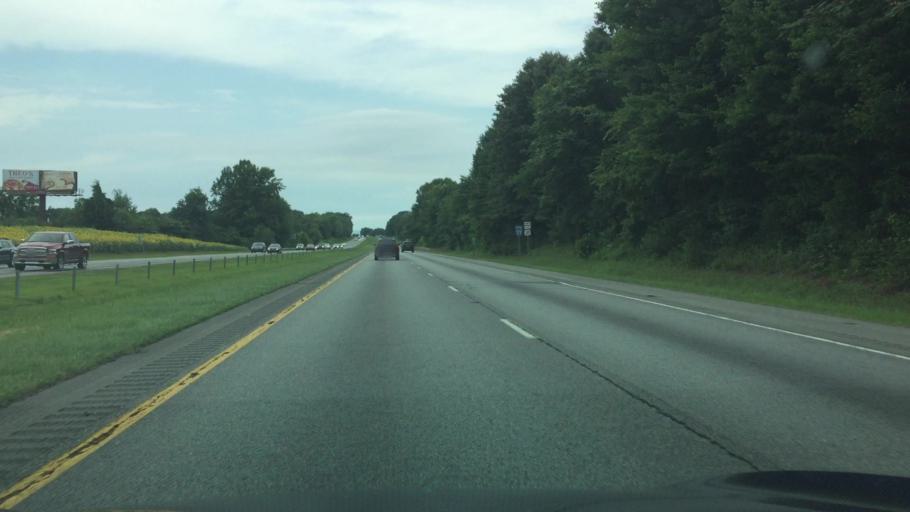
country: US
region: North Carolina
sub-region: Yadkin County
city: Jonesville
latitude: 36.1999
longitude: -80.8112
